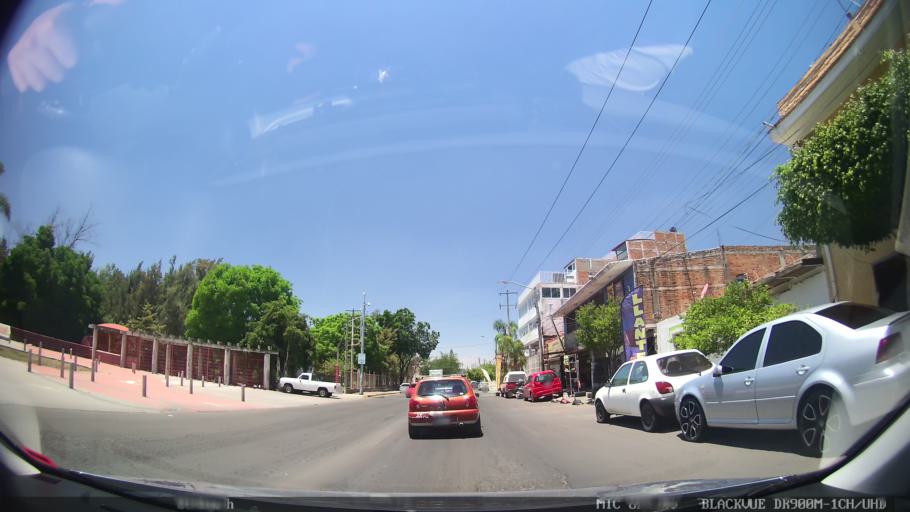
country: MX
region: Jalisco
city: Tlaquepaque
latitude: 20.6672
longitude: -103.2700
